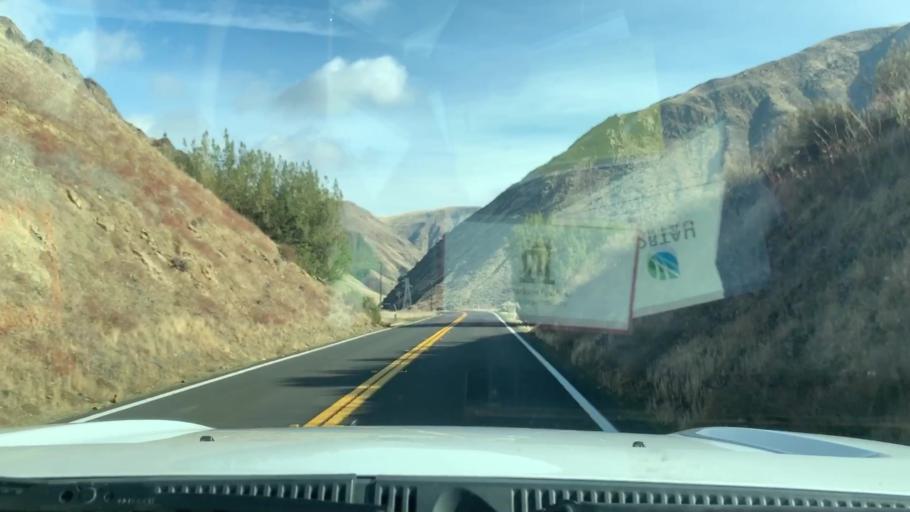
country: US
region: California
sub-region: Fresno County
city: Coalinga
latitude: 36.0929
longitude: -120.4789
